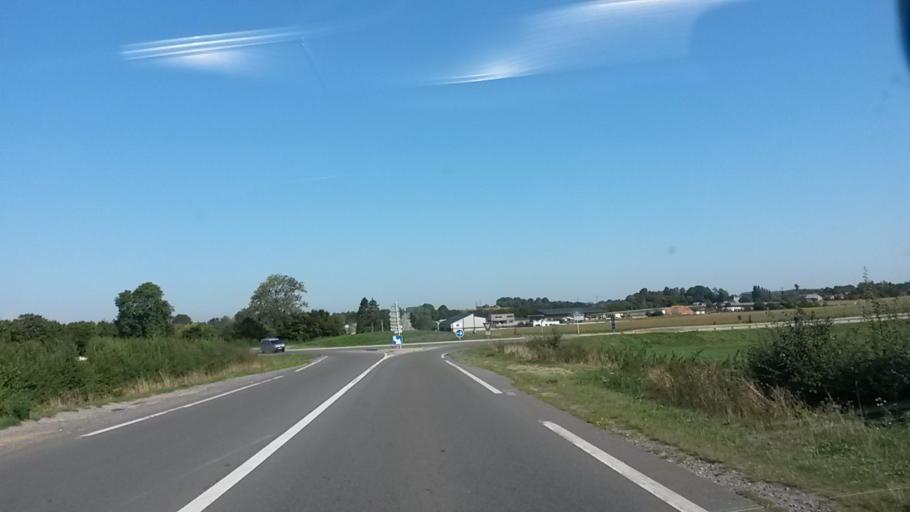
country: FR
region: Nord-Pas-de-Calais
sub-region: Departement du Nord
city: Hautmont
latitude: 50.2049
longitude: 3.9500
